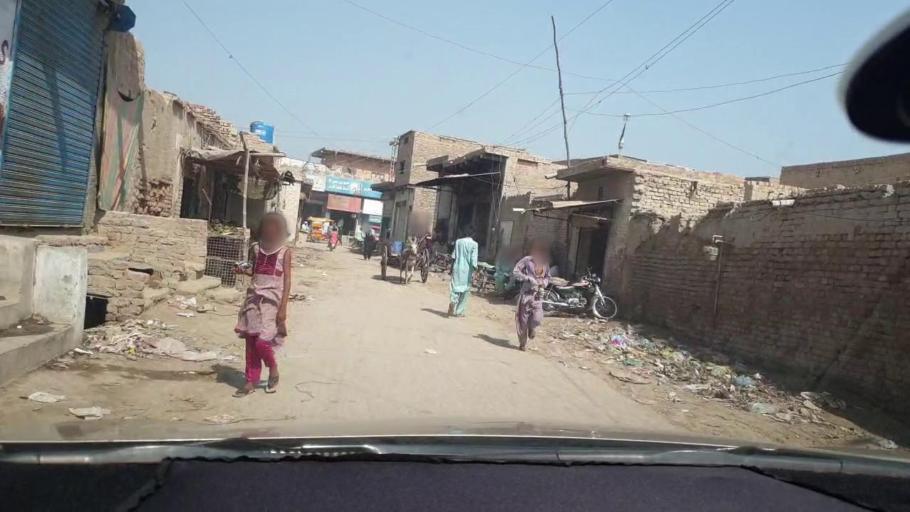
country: PK
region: Sindh
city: Kambar
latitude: 27.5851
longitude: 68.0015
